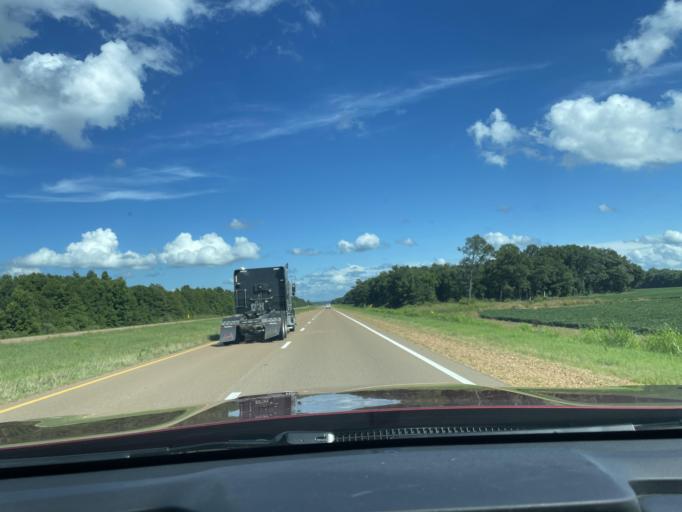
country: US
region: Mississippi
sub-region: Yazoo County
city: Yazoo City
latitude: 32.9701
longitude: -90.4468
